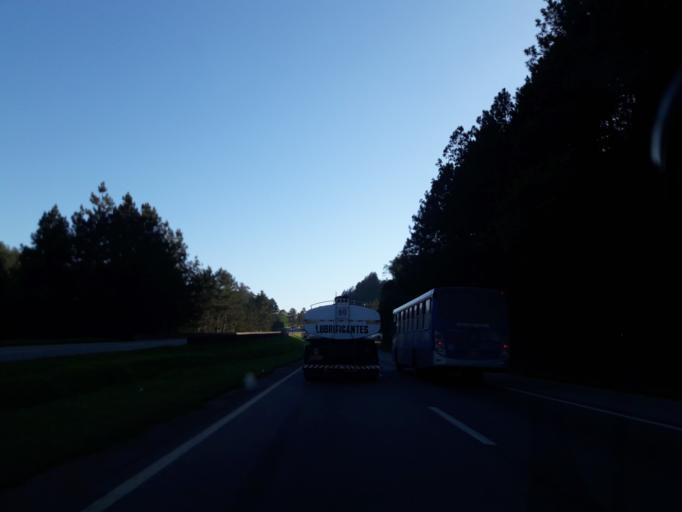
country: BR
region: Sao Paulo
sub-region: Juquitiba
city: Juquitiba
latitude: -23.9463
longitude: -47.0986
